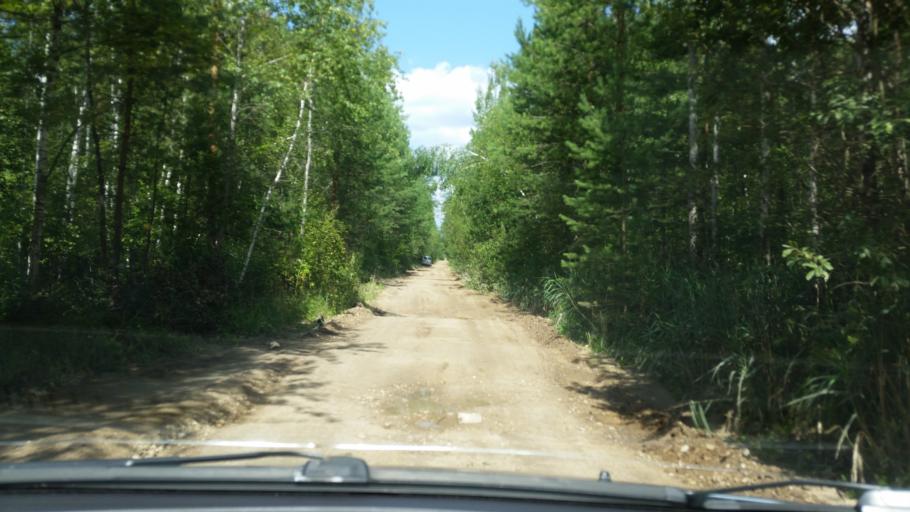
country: RU
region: Moskovskaya
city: Pushchino
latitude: 54.9061
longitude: 37.6857
